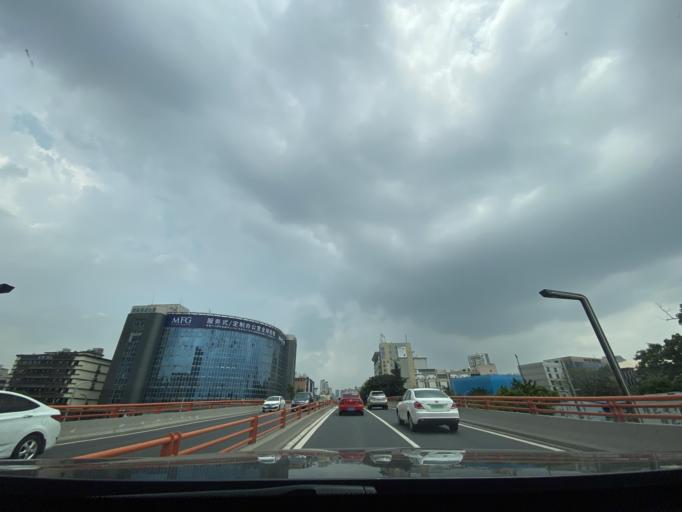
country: CN
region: Sichuan
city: Chengdu
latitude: 30.6355
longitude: 104.0737
